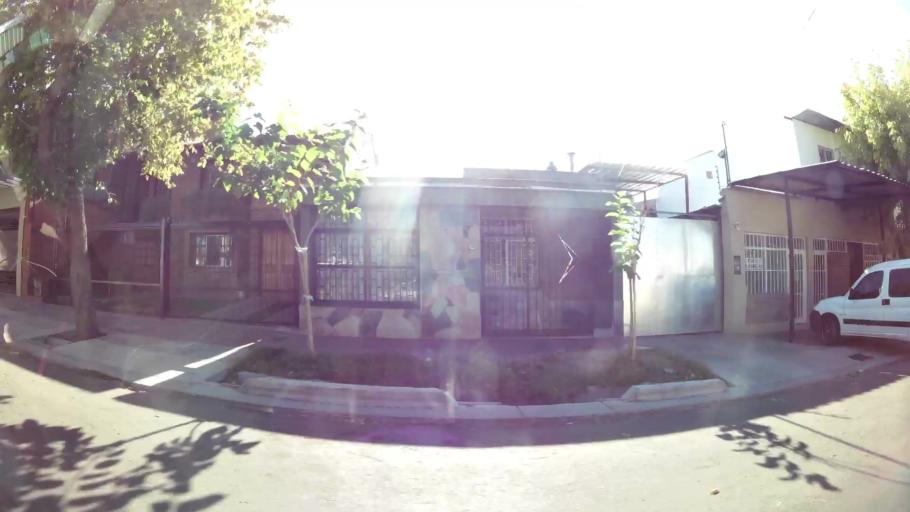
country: AR
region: Mendoza
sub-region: Departamento de Godoy Cruz
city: Godoy Cruz
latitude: -32.9109
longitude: -68.8338
